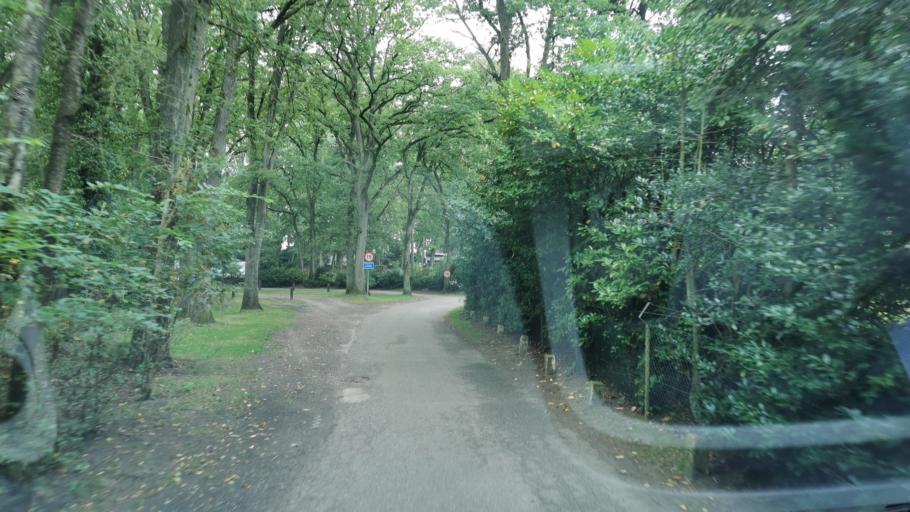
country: NL
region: Overijssel
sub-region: Gemeente Losser
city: Losser
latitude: 52.3218
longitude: 7.0286
